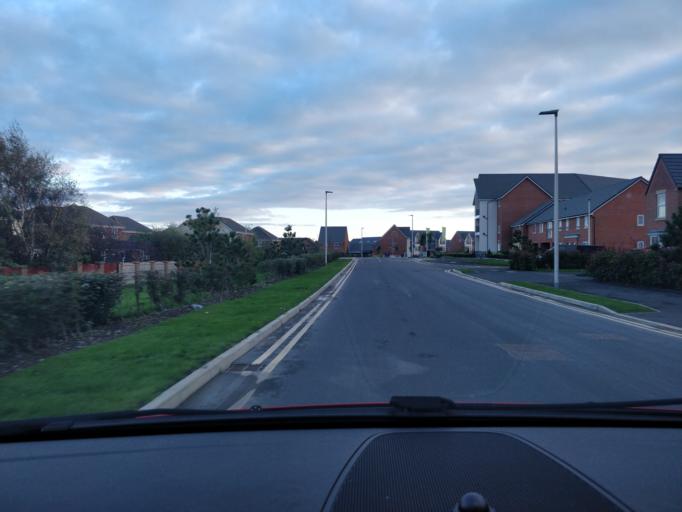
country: GB
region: England
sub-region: Sefton
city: Southport
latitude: 53.6290
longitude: -2.9829
